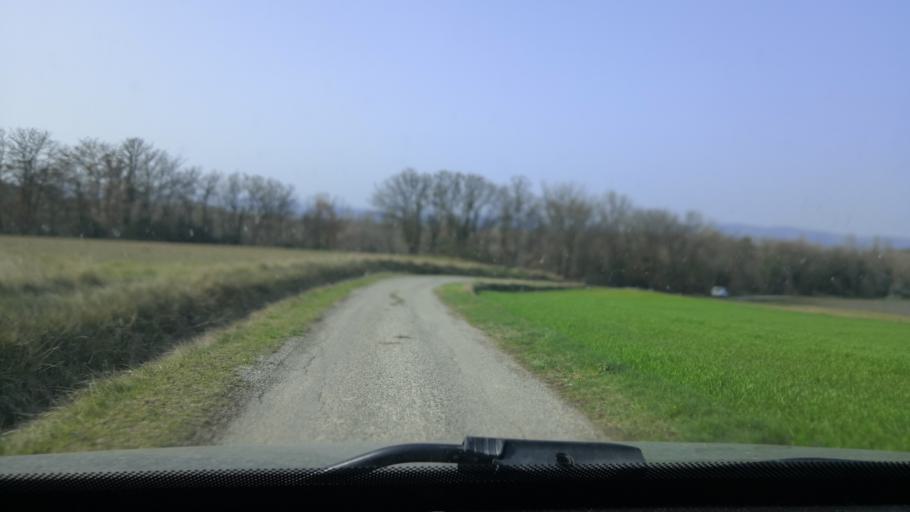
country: FR
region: Rhone-Alpes
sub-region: Departement de la Drome
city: La Begude-de-Mazenc
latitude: 44.5414
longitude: 4.9135
